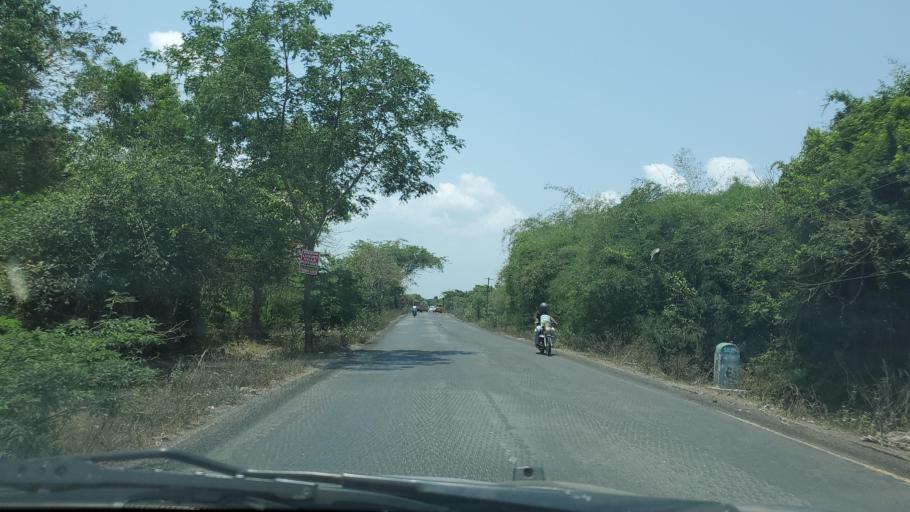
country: IN
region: Tamil Nadu
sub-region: Kancheepuram
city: Vengavasal
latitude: 12.8725
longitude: 80.1730
